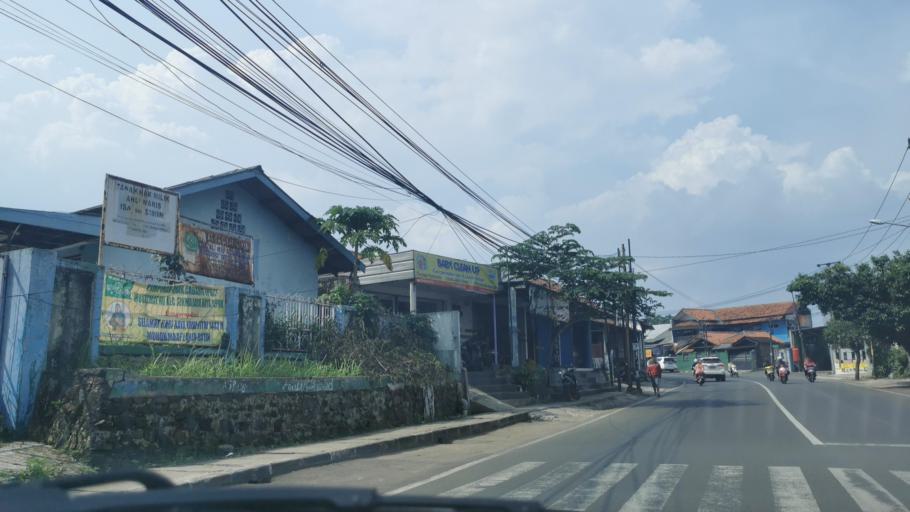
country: ID
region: West Java
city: Depok
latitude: -6.4052
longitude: 106.8370
